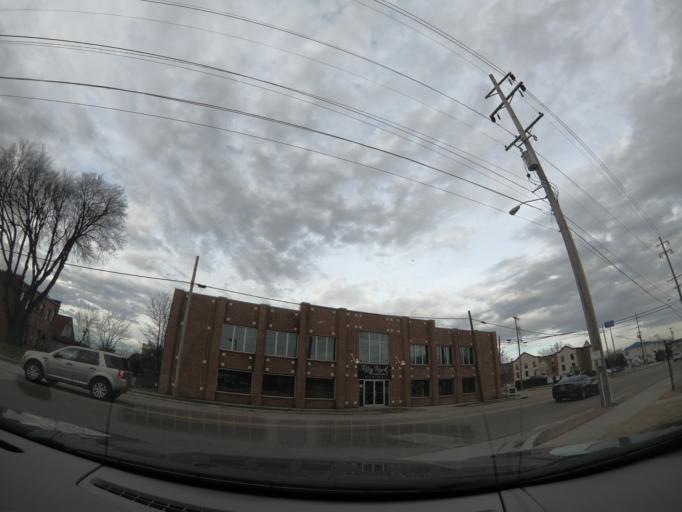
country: US
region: Tennessee
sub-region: Hamilton County
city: Chattanooga
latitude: 35.0283
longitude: -85.3158
